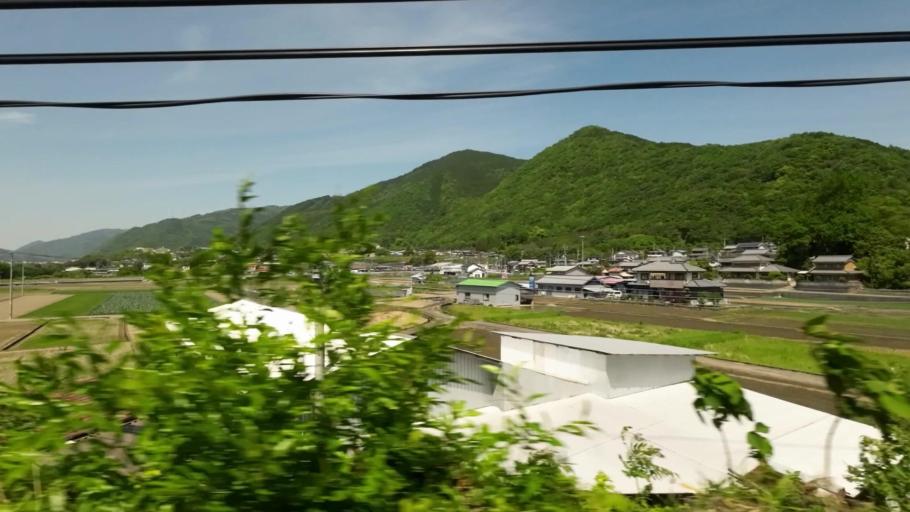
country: JP
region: Tokushima
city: Ikedacho
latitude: 34.0397
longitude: 133.8663
